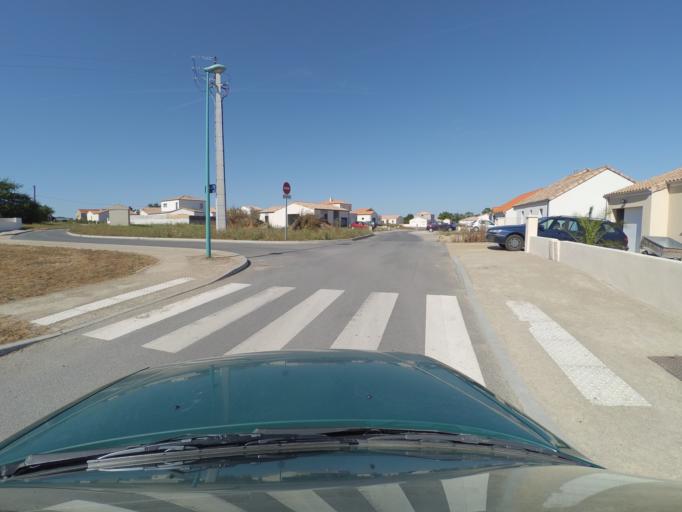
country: FR
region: Pays de la Loire
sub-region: Departement de la Loire-Atlantique
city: Aigrefeuille-sur-Maine
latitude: 47.0852
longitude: -1.4104
